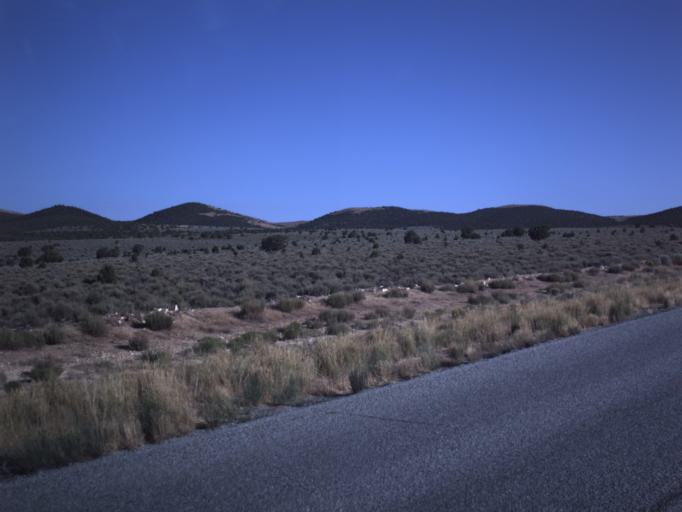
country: US
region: Utah
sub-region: Iron County
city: Parowan
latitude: 38.0235
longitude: -112.9981
